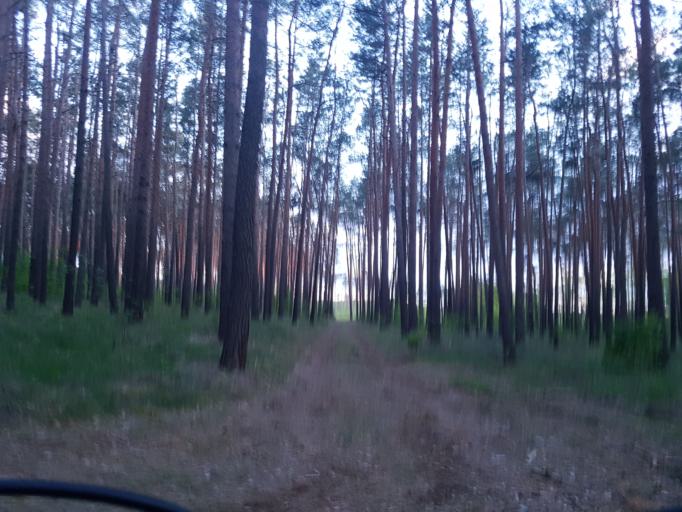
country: DE
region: Brandenburg
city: Schilda
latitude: 51.5646
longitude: 13.3758
